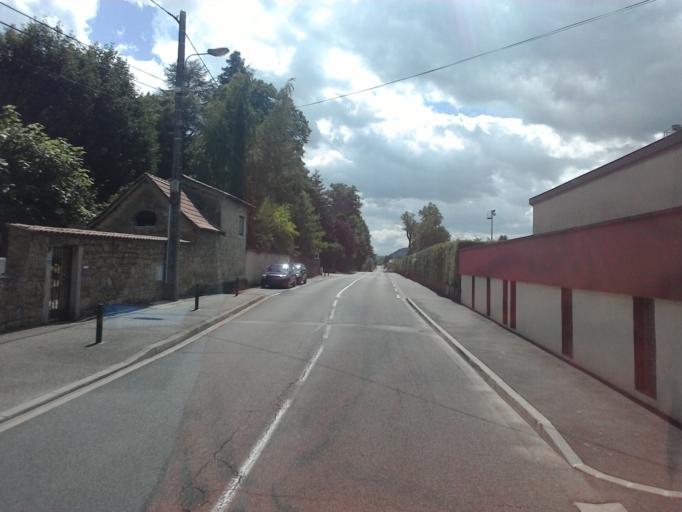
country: FR
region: Rhone-Alpes
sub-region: Departement de l'Ain
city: Lagnieu
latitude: 45.8994
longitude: 5.3527
